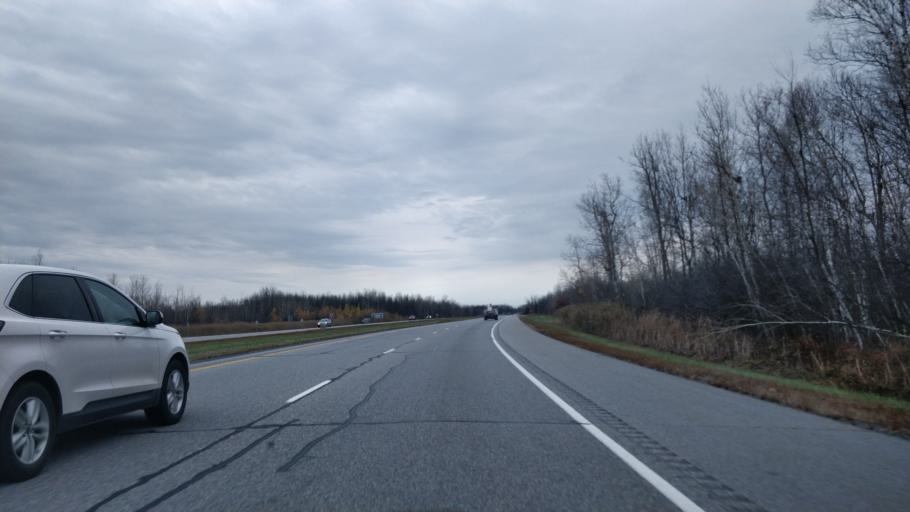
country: CA
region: Ontario
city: Bells Corners
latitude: 45.0792
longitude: -75.6307
